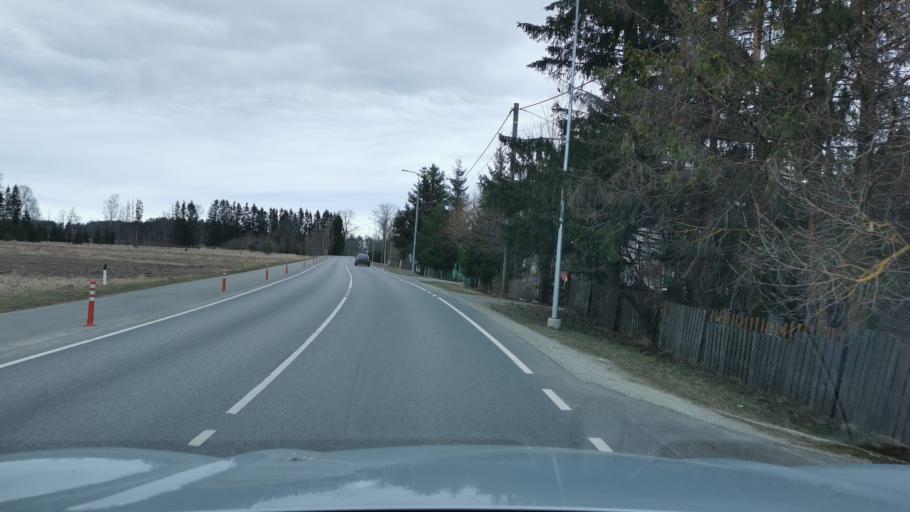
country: EE
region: Ida-Virumaa
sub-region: Puessi linn
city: Pussi
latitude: 59.3535
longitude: 27.0209
